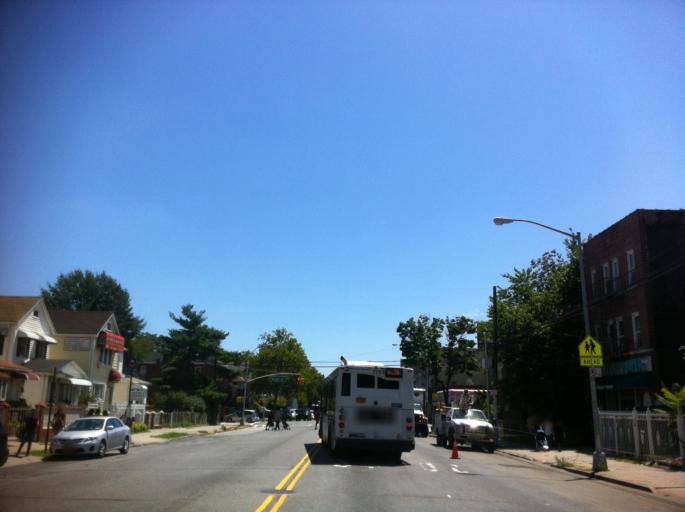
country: US
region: New York
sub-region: Bronx
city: The Bronx
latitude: 40.8292
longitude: -73.8610
